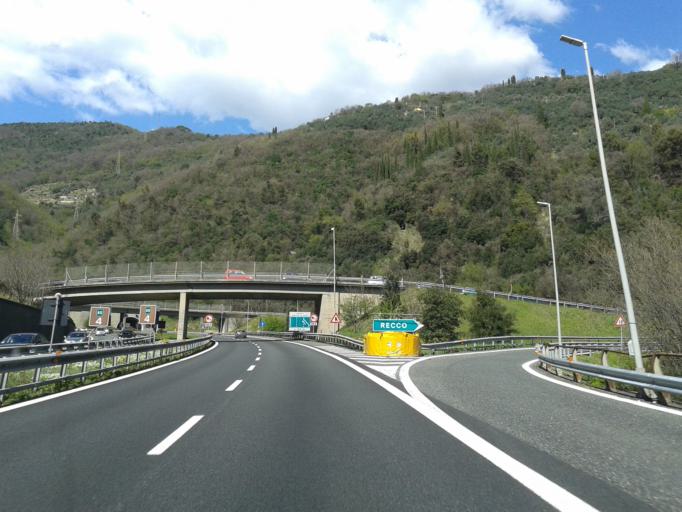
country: IT
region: Liguria
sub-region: Provincia di Genova
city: Avegno
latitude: 44.3767
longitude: 9.1456
